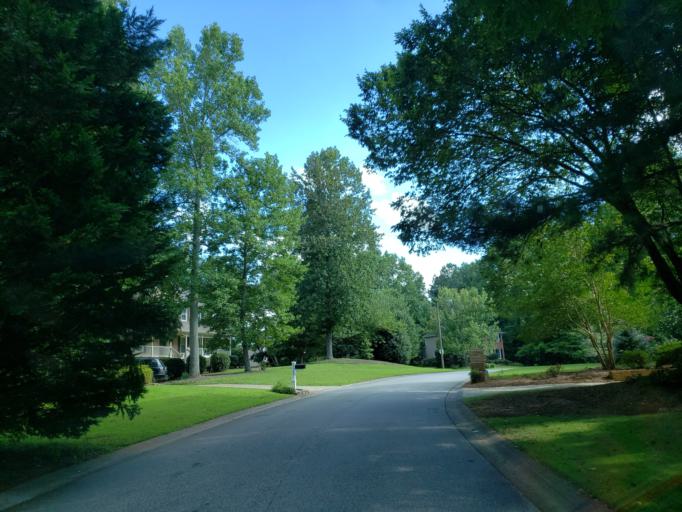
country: US
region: Georgia
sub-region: Cherokee County
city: Holly Springs
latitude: 34.1762
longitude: -84.4241
